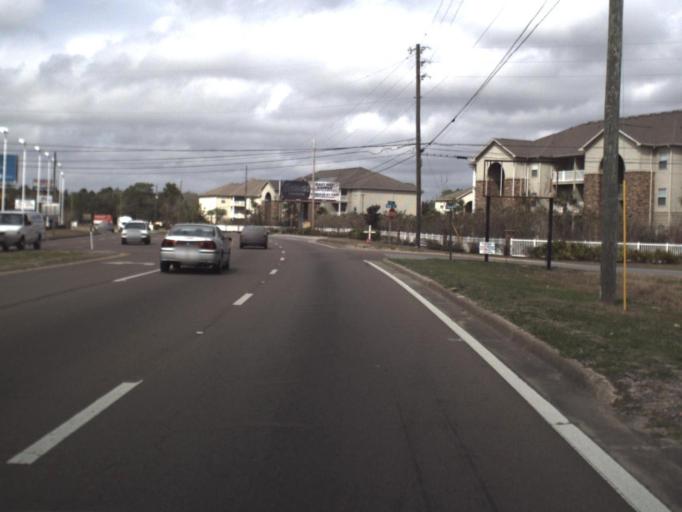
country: US
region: Florida
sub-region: Bay County
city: Springfield
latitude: 30.1725
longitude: -85.5922
